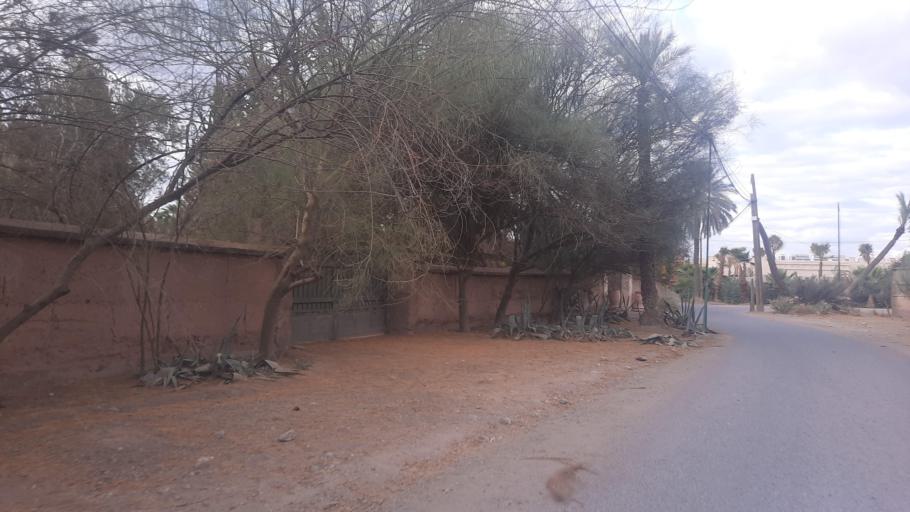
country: MA
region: Marrakech-Tensift-Al Haouz
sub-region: Marrakech
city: Marrakesh
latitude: 31.6753
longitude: -7.9531
